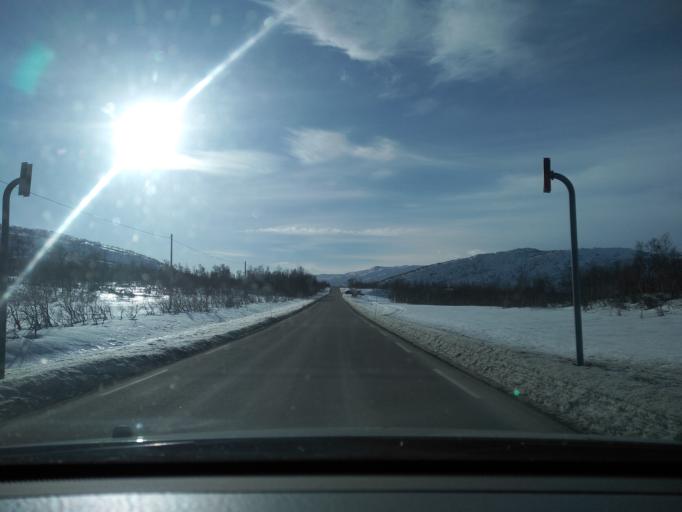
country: NO
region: Aust-Agder
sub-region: Bykle
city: Hovden
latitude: 59.6493
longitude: 7.4725
